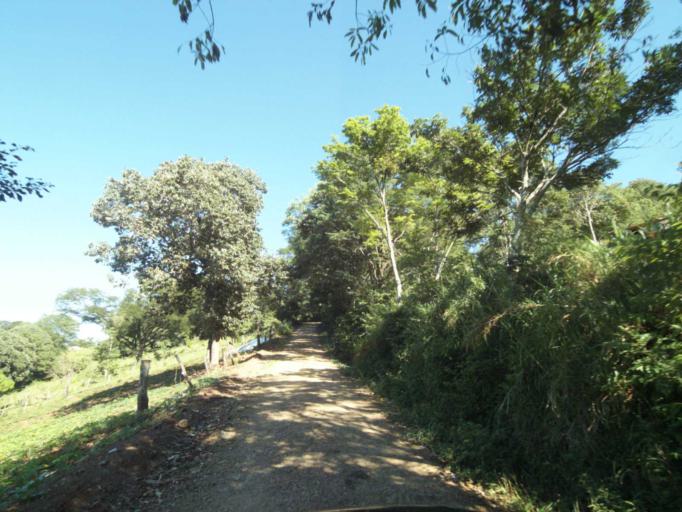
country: BR
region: Parana
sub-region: Francisco Beltrao
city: Francisco Beltrao
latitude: -26.1414
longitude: -53.3079
